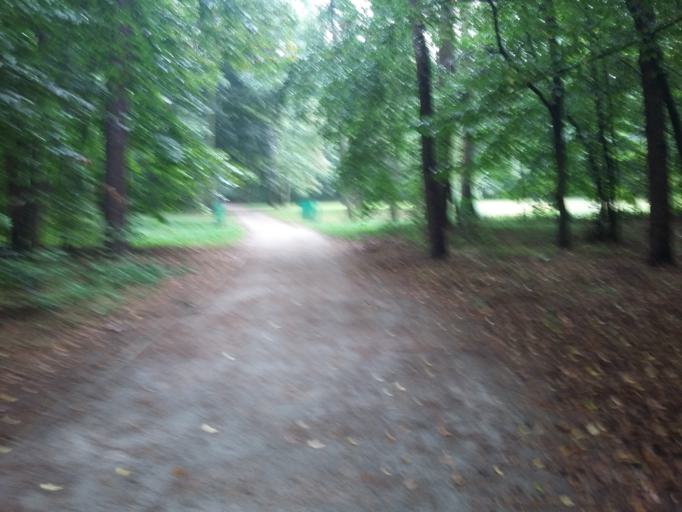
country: PL
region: Lodz Voivodeship
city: Lodz
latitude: 51.7653
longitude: 19.4056
